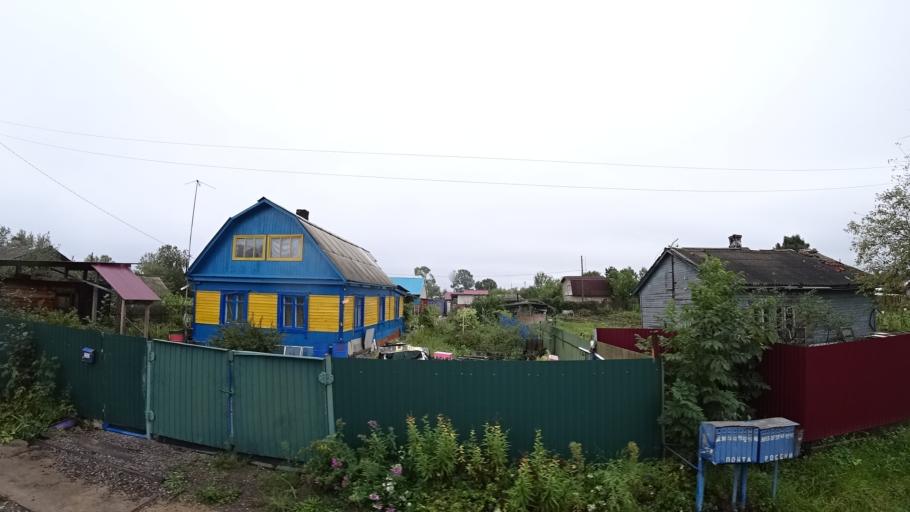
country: RU
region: Primorskiy
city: Monastyrishche
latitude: 44.1910
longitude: 132.4218
